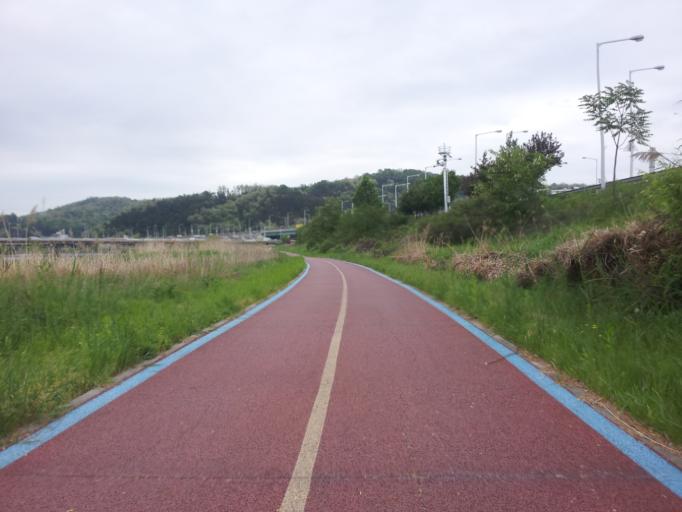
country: KR
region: Daejeon
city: Daejeon
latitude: 36.3760
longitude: 127.4076
